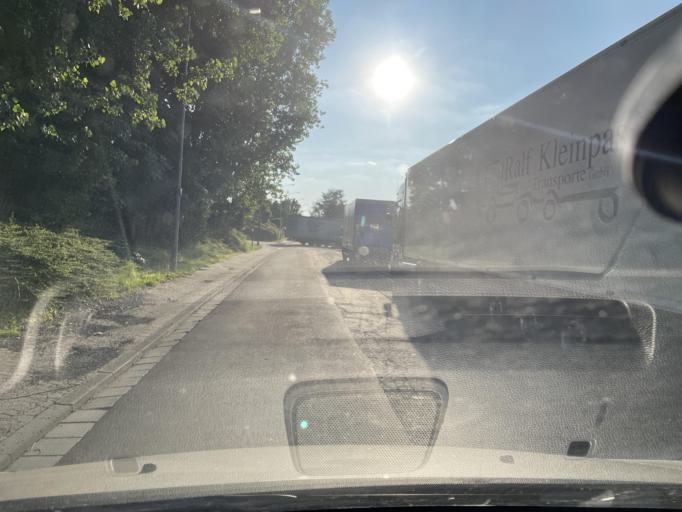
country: DE
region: Saarland
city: Sankt Ingbert
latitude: 49.2682
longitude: 7.1293
